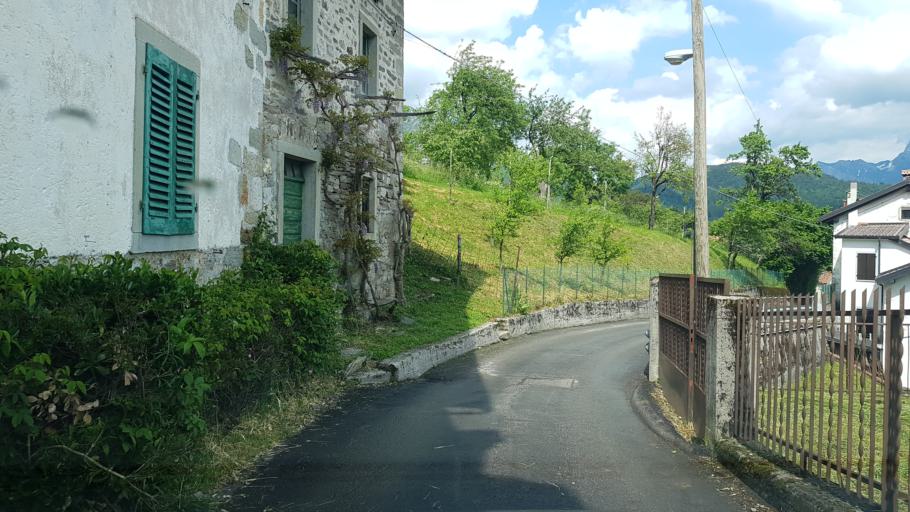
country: IT
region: Friuli Venezia Giulia
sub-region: Provincia di Udine
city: Arta Terme
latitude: 46.4707
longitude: 13.0039
